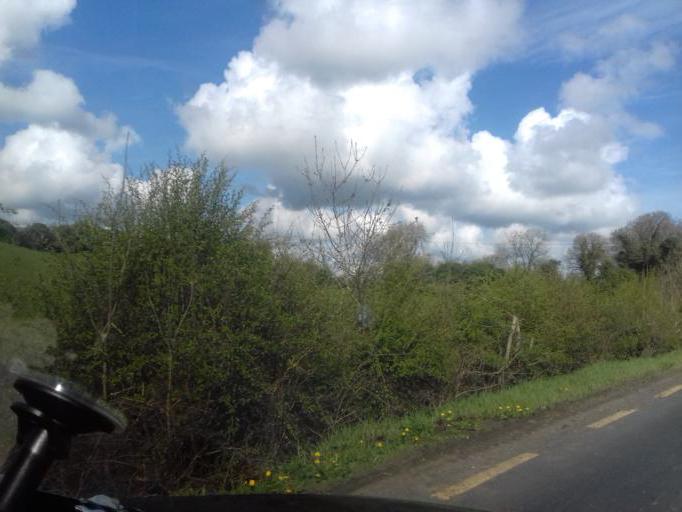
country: IE
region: Ulster
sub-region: An Cabhan
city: Virginia
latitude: 53.8505
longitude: -7.1013
